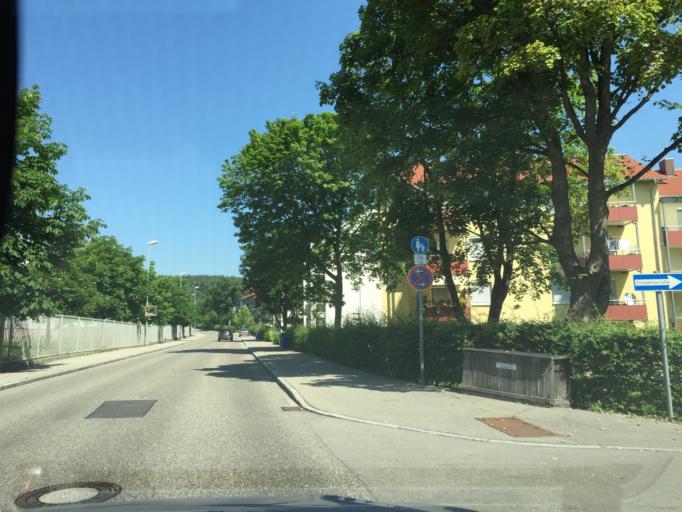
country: DE
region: Baden-Wuerttemberg
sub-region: Tuebingen Region
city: Ulm
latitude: 48.4122
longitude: 9.9650
